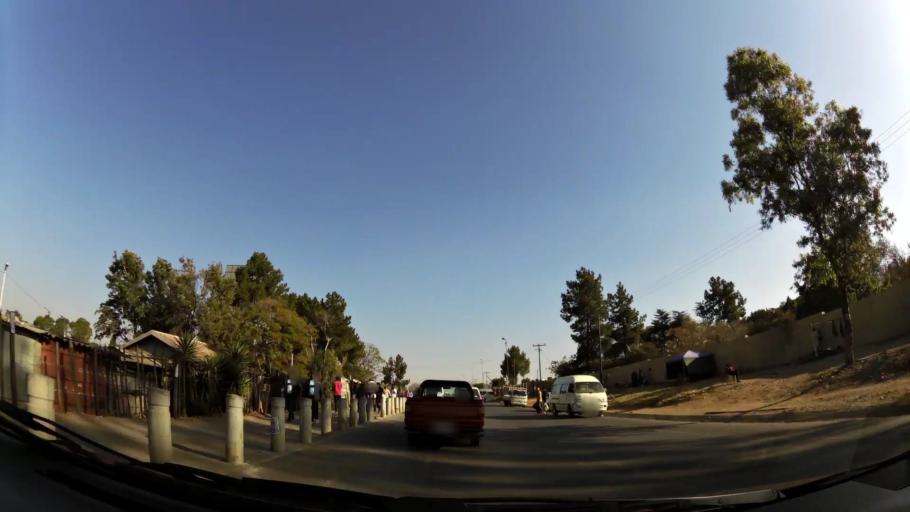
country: ZA
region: Gauteng
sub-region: West Rand District Municipality
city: Muldersdriseloop
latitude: -26.0572
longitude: 27.9033
